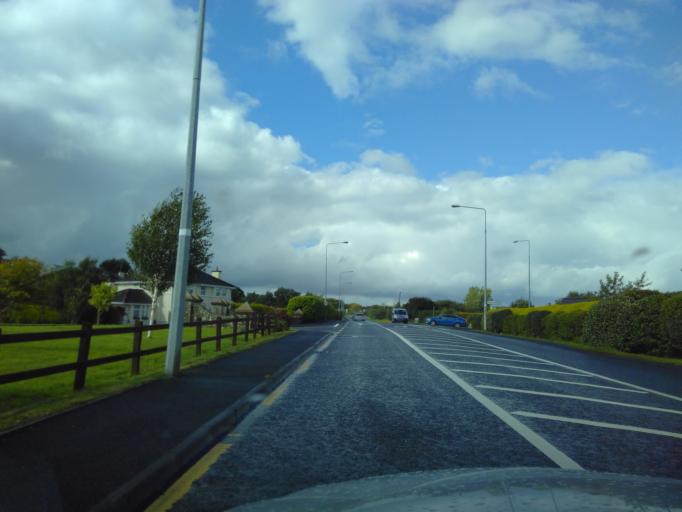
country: IE
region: Ulster
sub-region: County Donegal
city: Letterkenny
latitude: 54.9595
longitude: -7.6925
